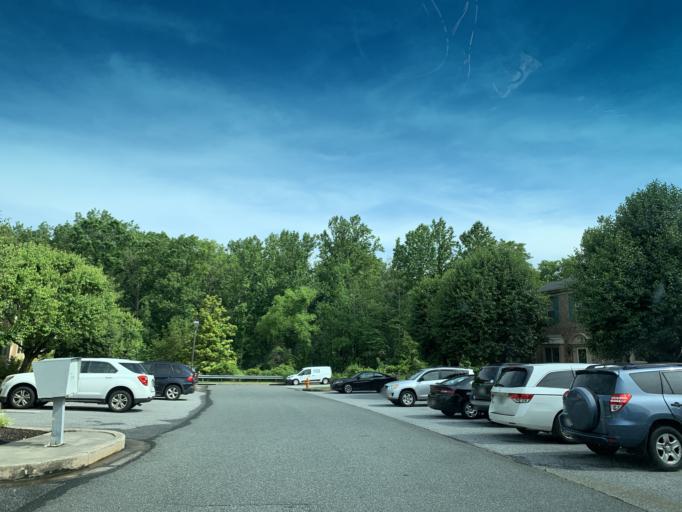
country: US
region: Maryland
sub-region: Baltimore County
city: Perry Hall
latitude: 39.3913
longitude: -76.4724
